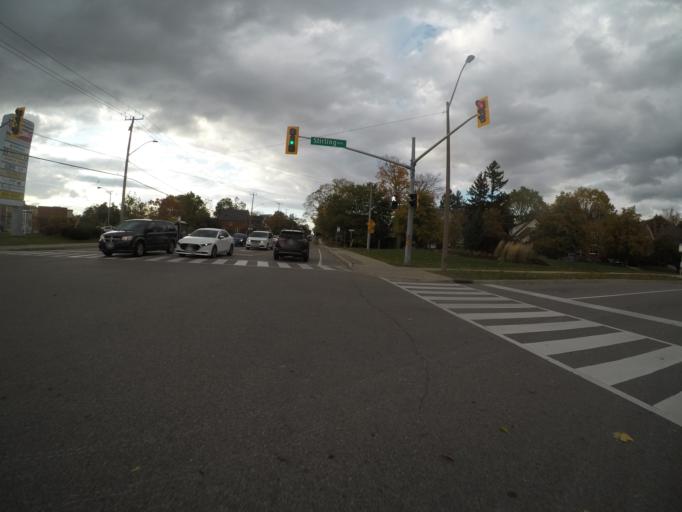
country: CA
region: Ontario
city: Kitchener
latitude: 43.4412
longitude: -80.4842
